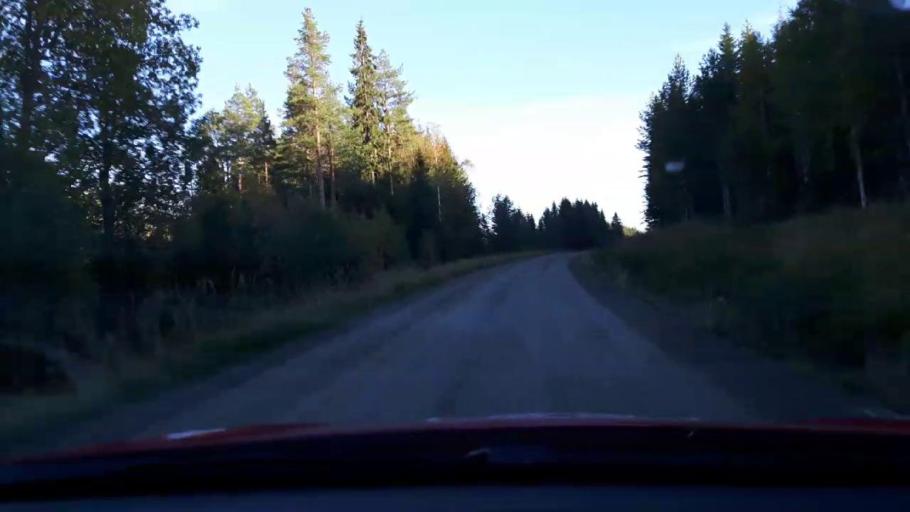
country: SE
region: Jaemtland
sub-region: OEstersunds Kommun
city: Brunflo
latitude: 62.9441
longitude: 14.9857
